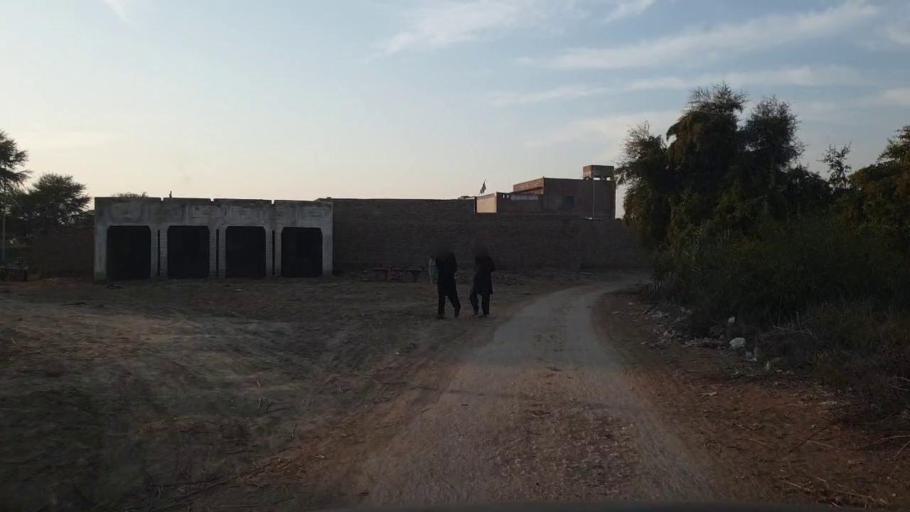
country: PK
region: Sindh
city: Shahpur Chakar
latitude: 26.1785
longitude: 68.6152
